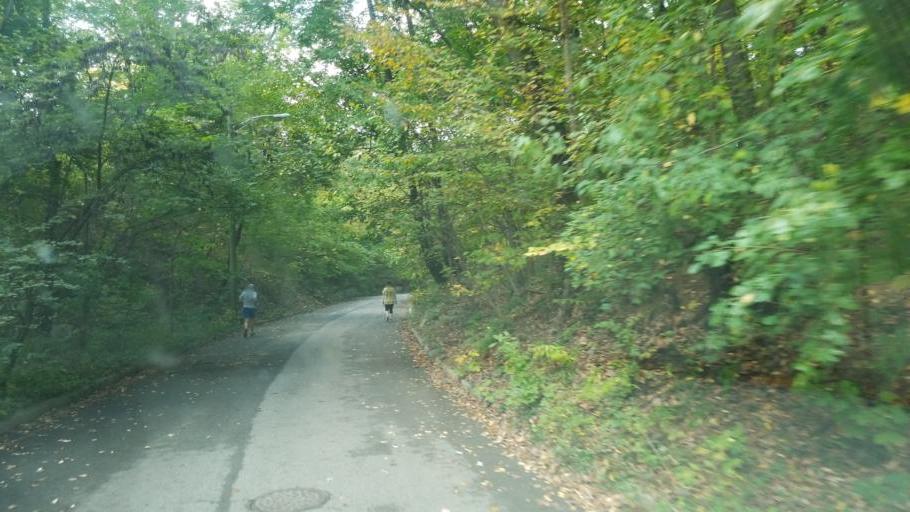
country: US
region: Ohio
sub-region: Franklin County
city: Grandview Heights
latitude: 40.0251
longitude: -83.0100
